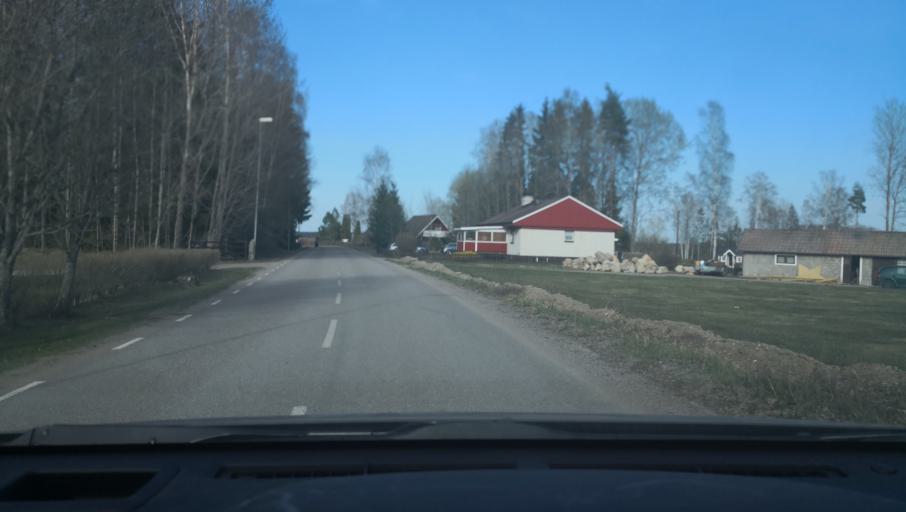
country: SE
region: Uppsala
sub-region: Heby Kommun
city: Heby
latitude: 59.9234
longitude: 16.8514
